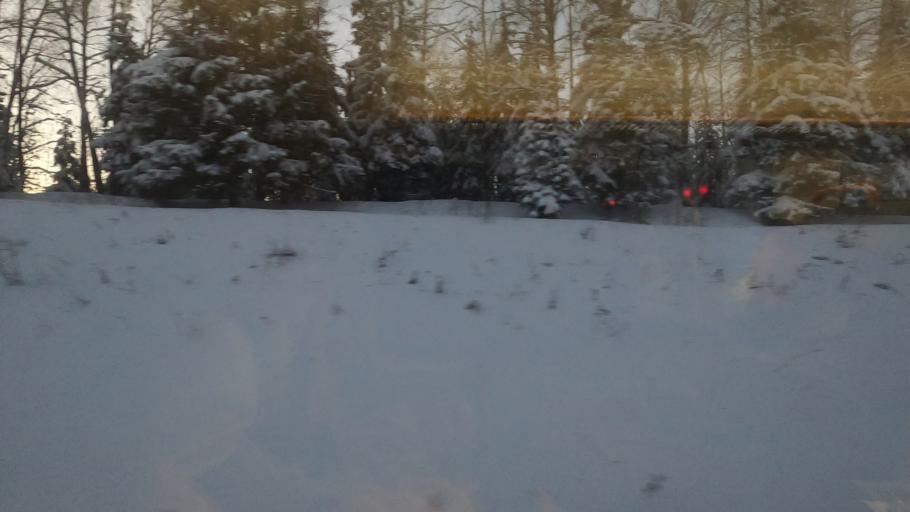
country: RU
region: Moskovskaya
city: Lugovaya
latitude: 56.0604
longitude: 37.4870
